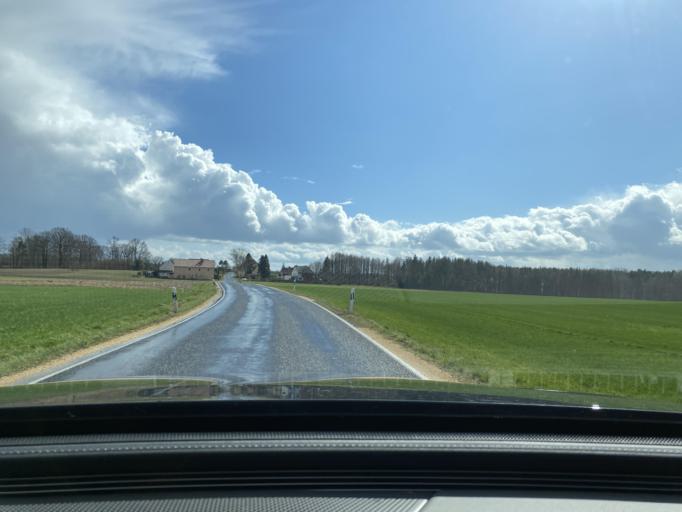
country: DE
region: Saxony
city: Radibor
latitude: 51.2648
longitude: 14.4284
